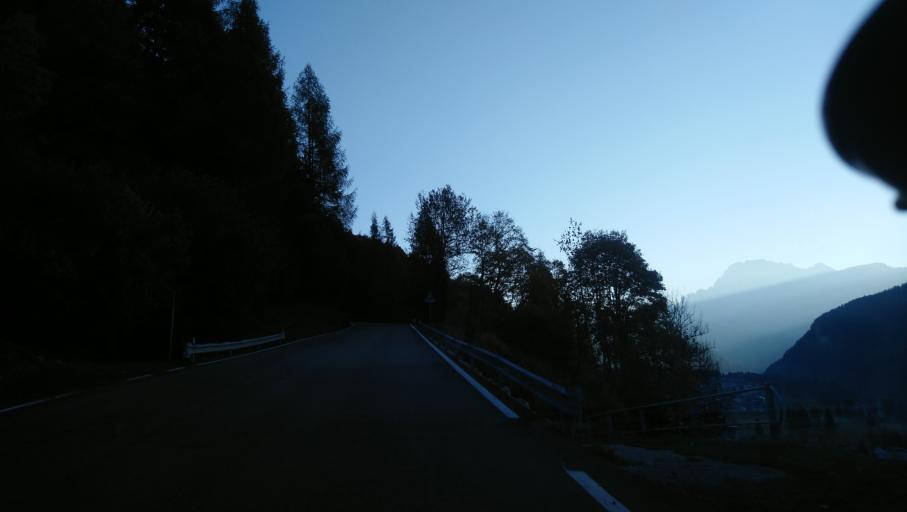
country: IT
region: Veneto
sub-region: Provincia di Belluno
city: Falcade Alto
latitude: 46.3559
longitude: 11.8615
